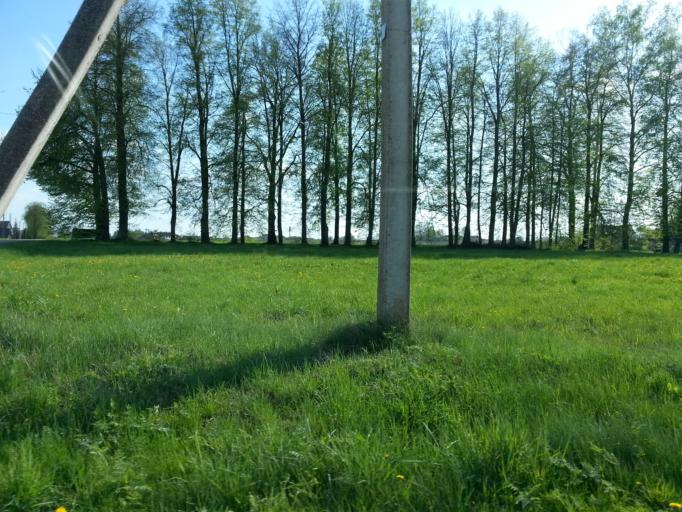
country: LT
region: Panevezys
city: Pasvalys
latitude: 56.0323
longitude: 24.3593
